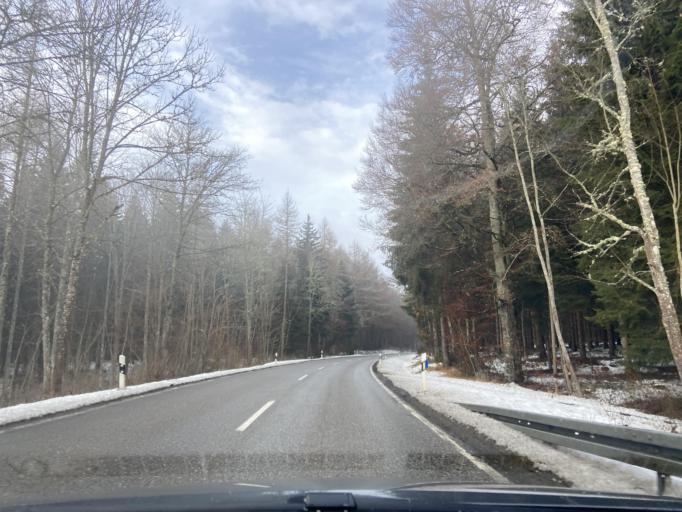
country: DE
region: Baden-Wuerttemberg
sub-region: Tuebingen Region
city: Hettingen
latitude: 48.2381
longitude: 9.2627
